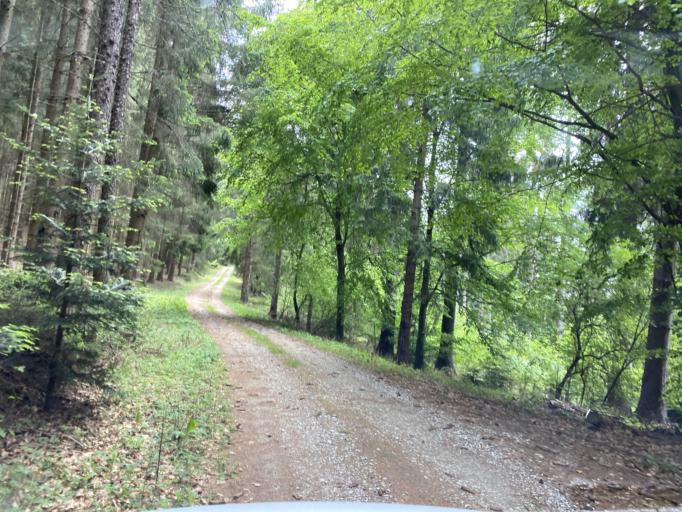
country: AT
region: Styria
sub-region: Politischer Bezirk Weiz
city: Koglhof
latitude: 47.3091
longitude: 15.7037
